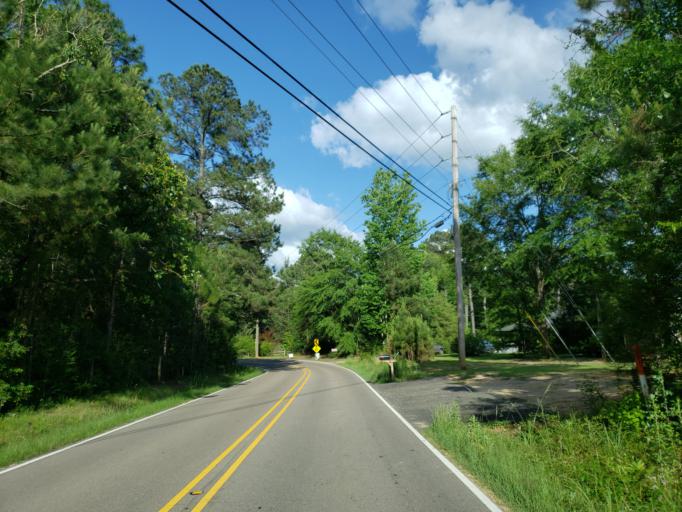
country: US
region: Mississippi
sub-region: Lamar County
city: West Hattiesburg
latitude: 31.2706
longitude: -89.4099
